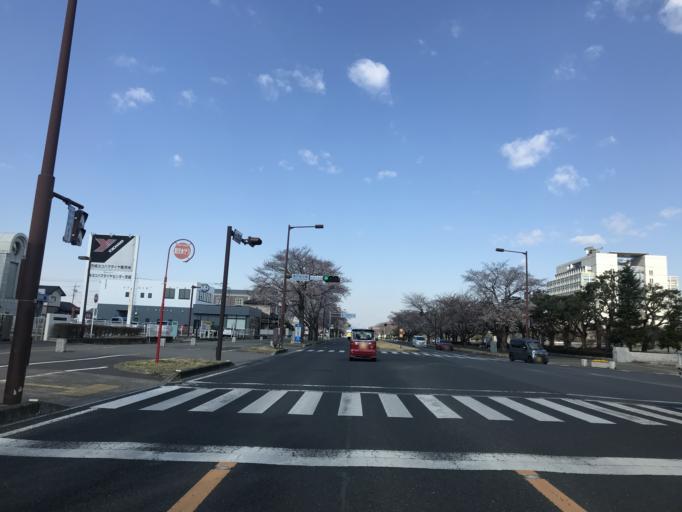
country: JP
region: Ibaraki
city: Mito-shi
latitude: 36.3390
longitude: 140.4485
